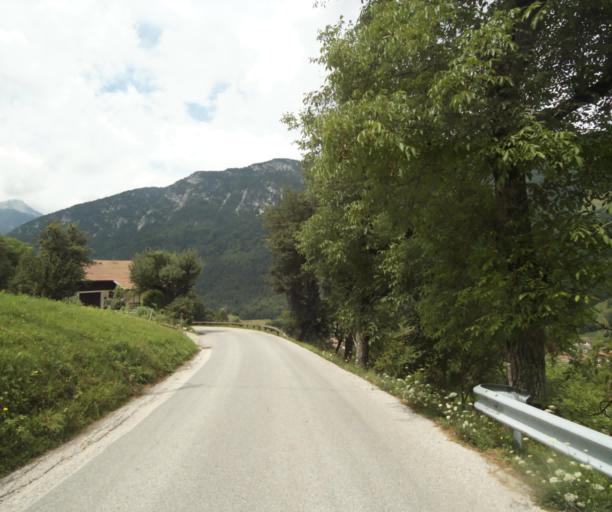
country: FR
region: Rhone-Alpes
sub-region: Departement de la Haute-Savoie
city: Thones
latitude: 45.8940
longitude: 6.3488
